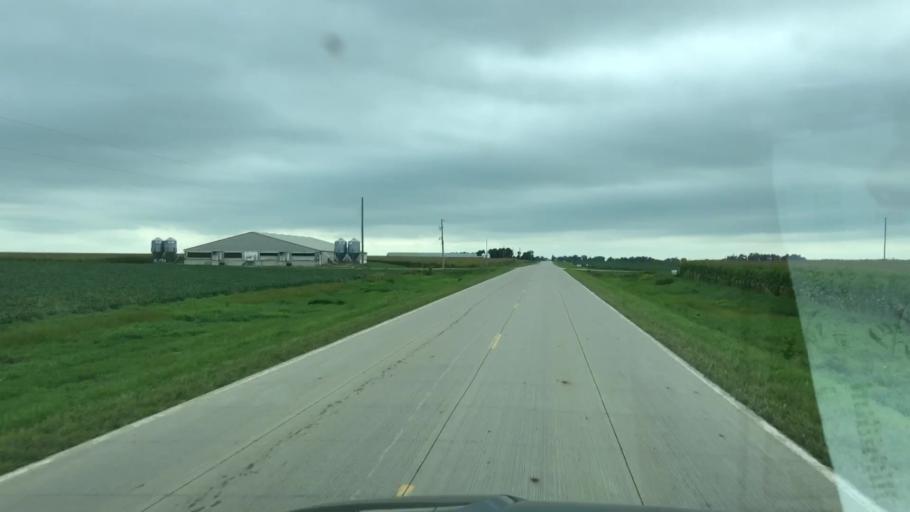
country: US
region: Iowa
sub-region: O'Brien County
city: Sheldon
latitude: 43.1289
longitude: -95.9790
